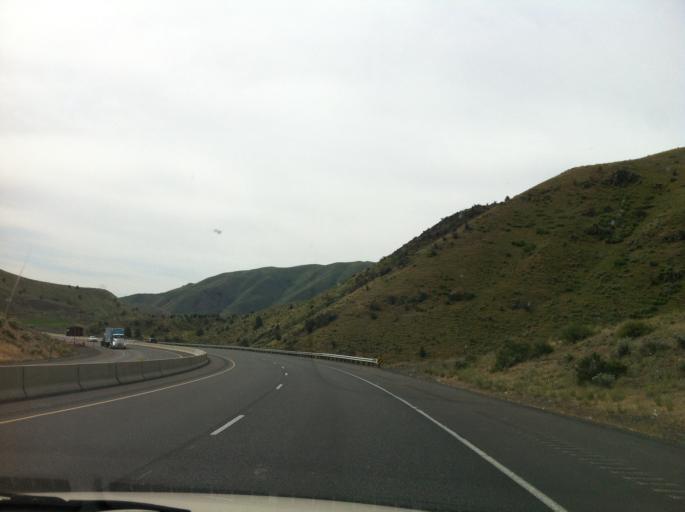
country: US
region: Idaho
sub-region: Washington County
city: Weiser
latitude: 44.5119
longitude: -117.3765
